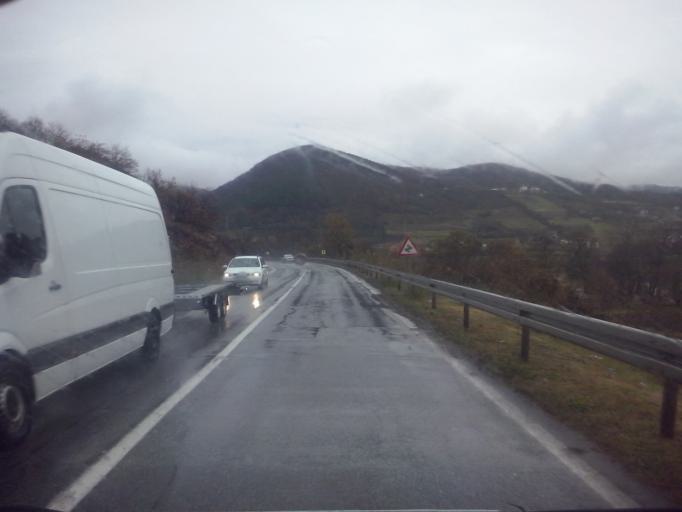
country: RS
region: Central Serbia
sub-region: Raski Okrug
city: Raska
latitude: 43.3314
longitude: 20.6326
